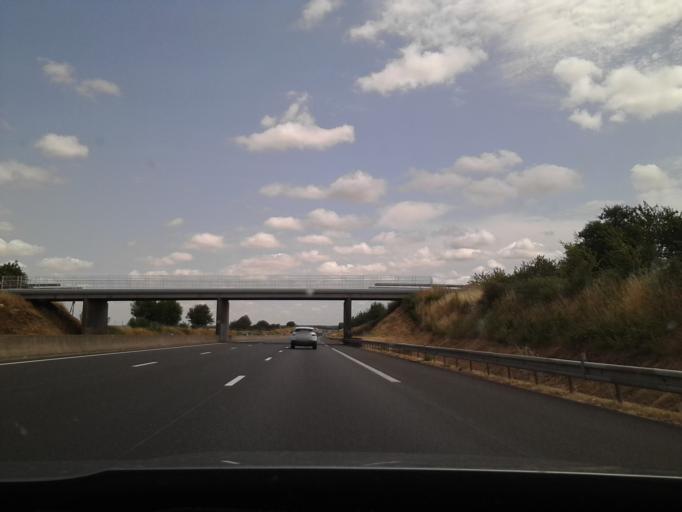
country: FR
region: Centre
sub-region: Departement d'Indre-et-Loire
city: Reugny
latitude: 47.5027
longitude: 0.8623
